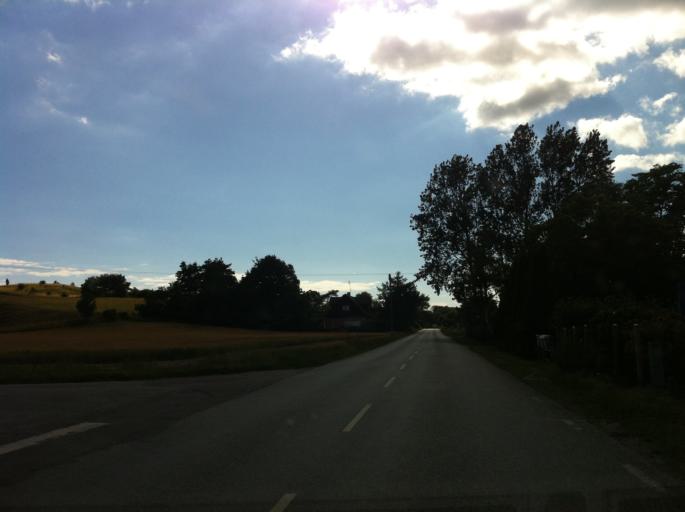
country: SE
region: Skane
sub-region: Ystads Kommun
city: Kopingebro
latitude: 55.3954
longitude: 14.0378
